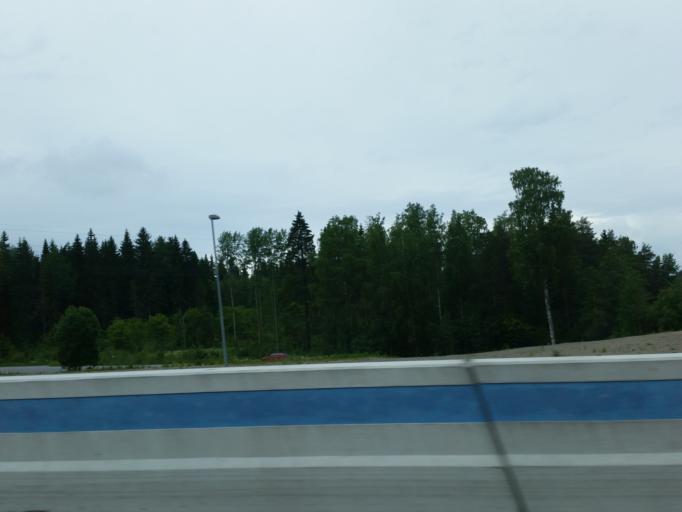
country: FI
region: Northern Savo
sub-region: Kuopio
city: Kuopio
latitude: 62.9513
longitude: 27.6770
